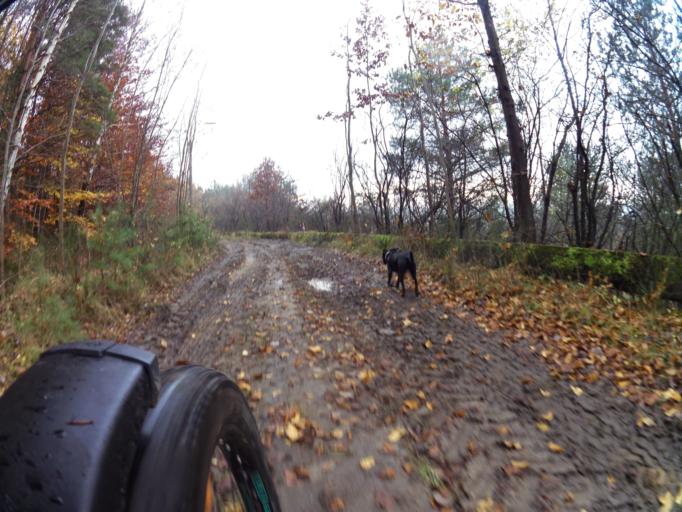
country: PL
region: Pomeranian Voivodeship
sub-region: Powiat pucki
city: Krokowa
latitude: 54.7421
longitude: 18.0989
